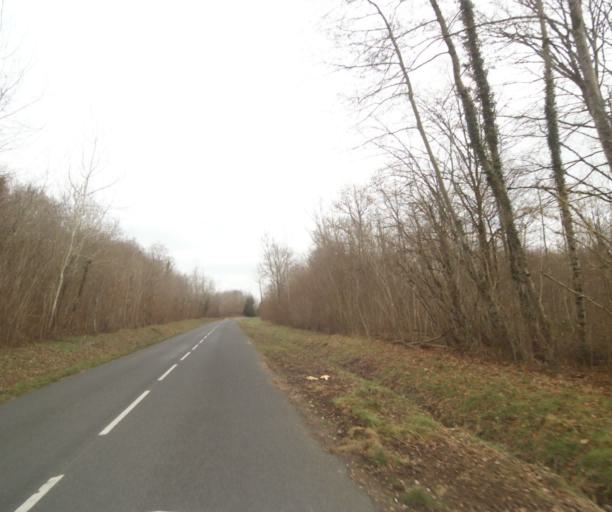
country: FR
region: Champagne-Ardenne
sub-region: Departement de la Marne
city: Sermaize-les-Bains
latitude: 48.7366
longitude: 4.8890
